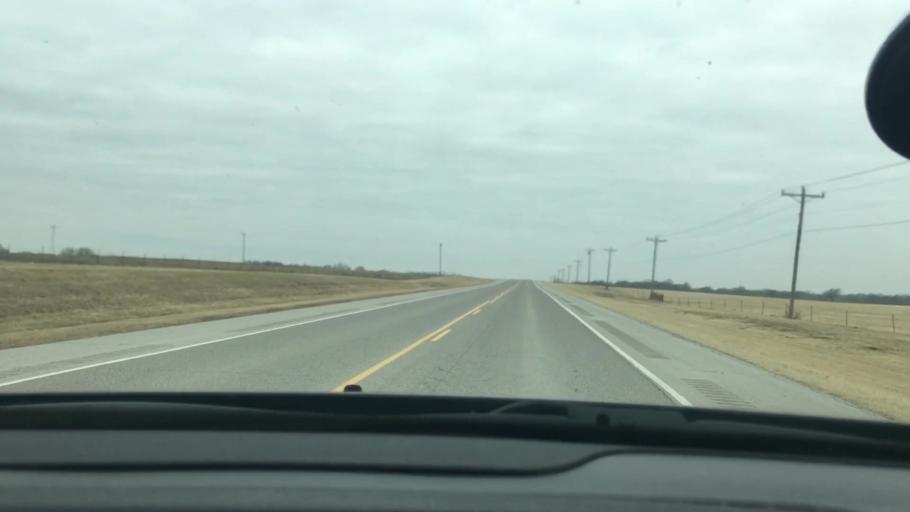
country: US
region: Oklahoma
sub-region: Murray County
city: Davis
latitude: 34.5214
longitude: -97.2940
